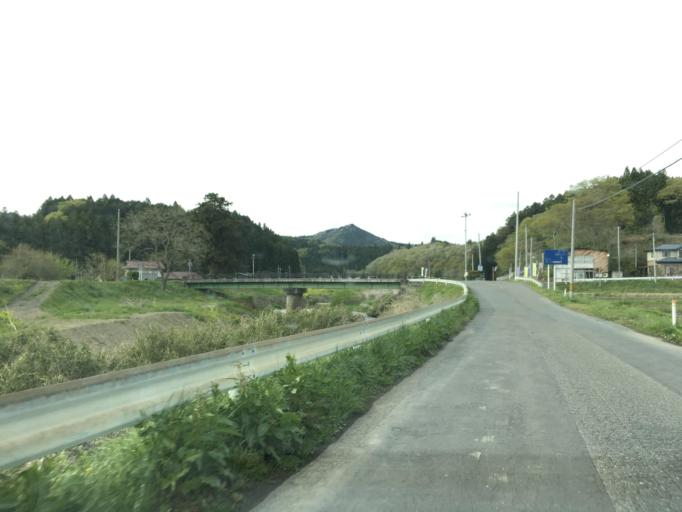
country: JP
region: Iwate
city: Ichinoseki
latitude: 38.8482
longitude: 141.3029
